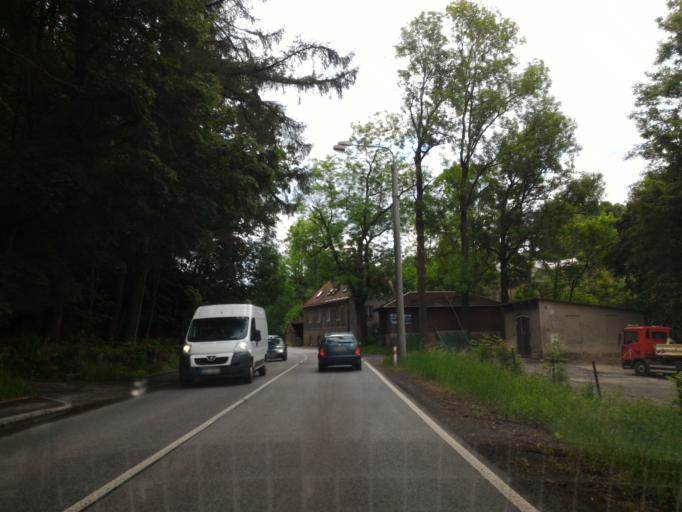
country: CZ
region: Liberecky
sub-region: Okres Jablonec nad Nisou
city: Jablonec nad Nisou
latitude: 50.7254
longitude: 15.1232
